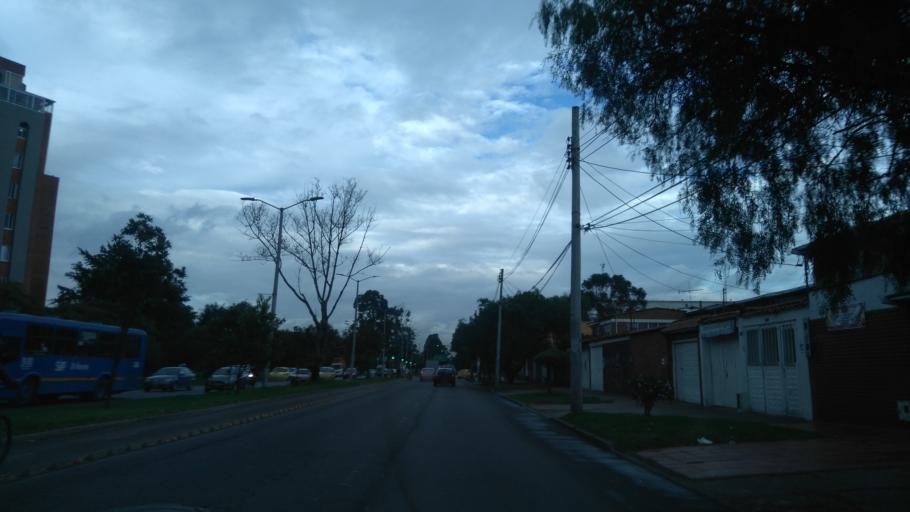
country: CO
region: Bogota D.C.
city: Bogota
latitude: 4.6432
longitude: -74.0893
